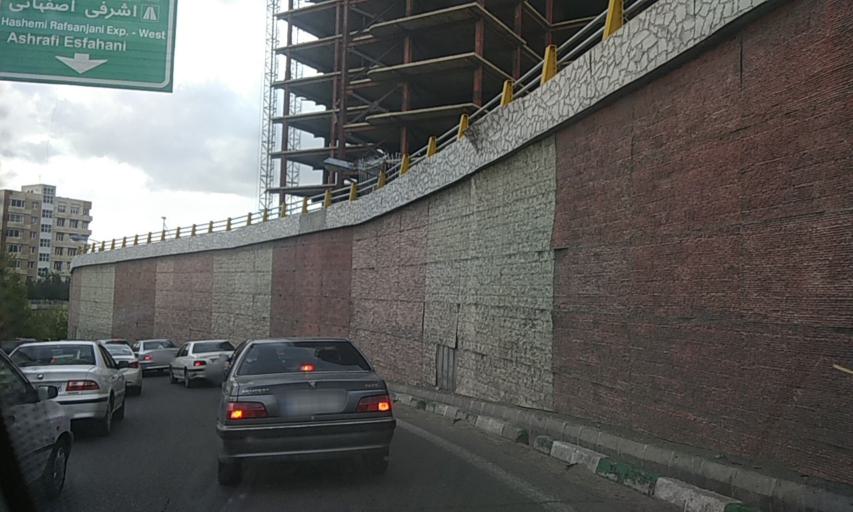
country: IR
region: Tehran
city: Tajrish
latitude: 35.7727
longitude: 51.3446
